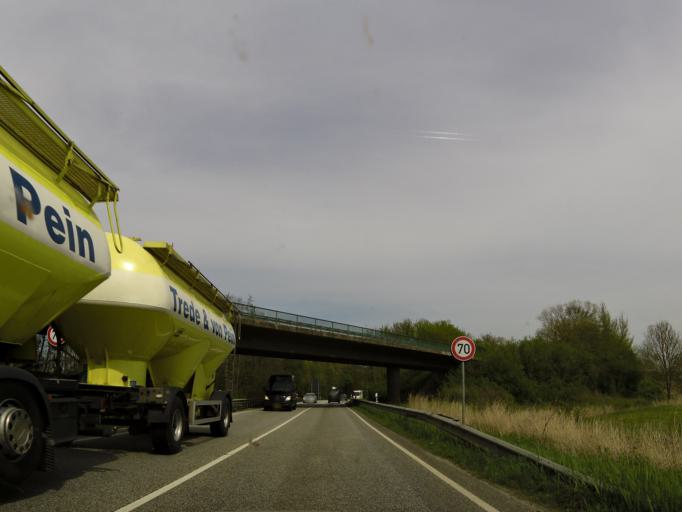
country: DE
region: Schleswig-Holstein
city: Tonning
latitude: 54.3290
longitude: 8.9542
